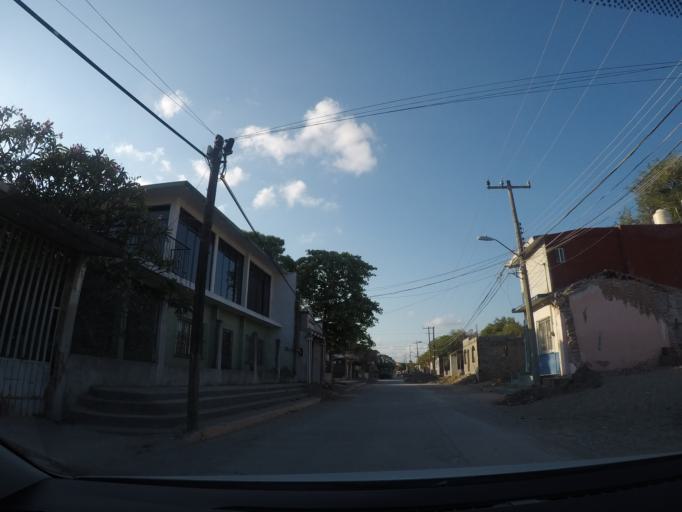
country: MX
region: Oaxaca
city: Juchitan de Zaragoza
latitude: 16.4353
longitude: -95.0265
